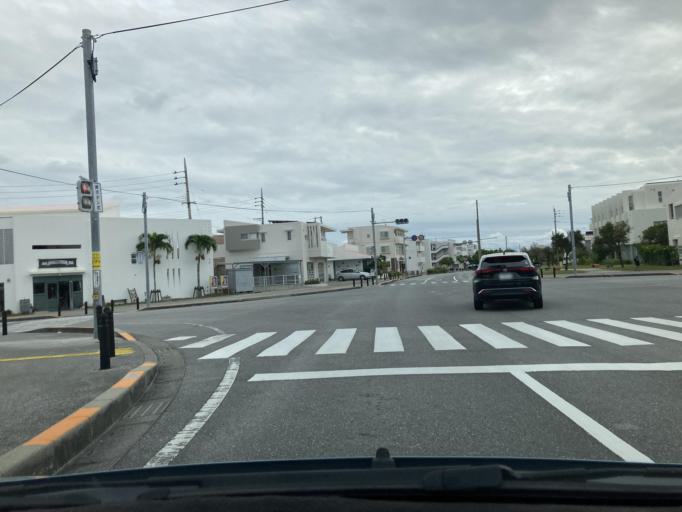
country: JP
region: Okinawa
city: Itoman
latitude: 26.1555
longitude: 127.6619
